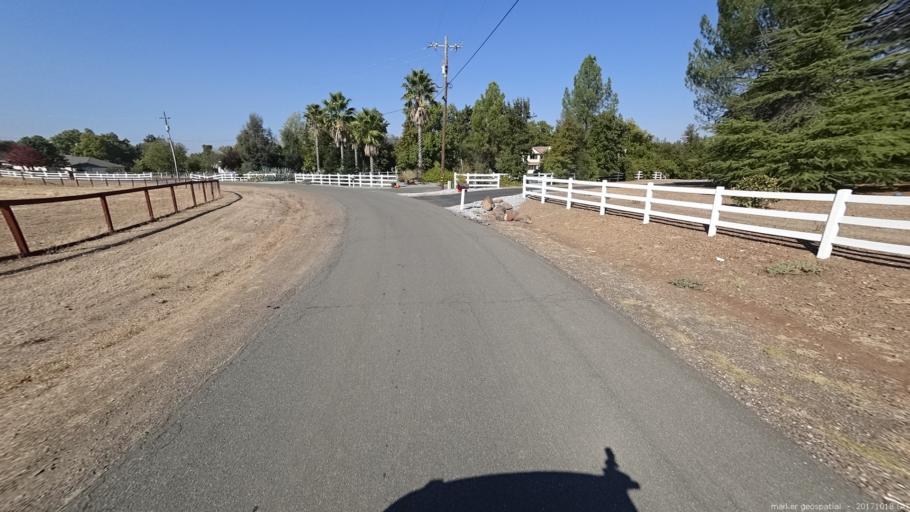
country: US
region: California
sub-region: Shasta County
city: Palo Cedro
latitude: 40.5432
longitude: -122.1716
